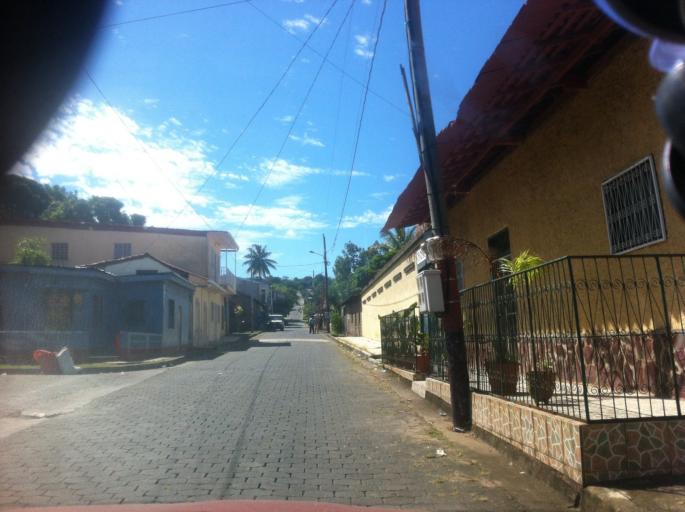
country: NI
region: Boaco
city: San Jose de los Remates
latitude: 12.6661
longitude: -85.7876
